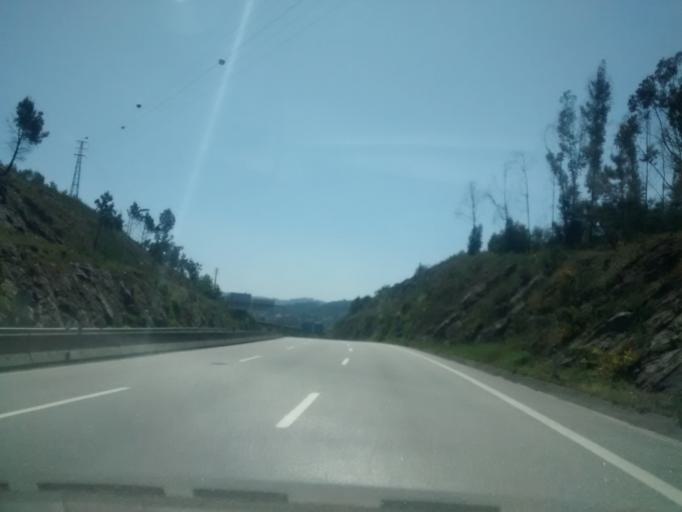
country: PT
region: Braga
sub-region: Braga
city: Braga
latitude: 41.5144
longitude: -8.4449
